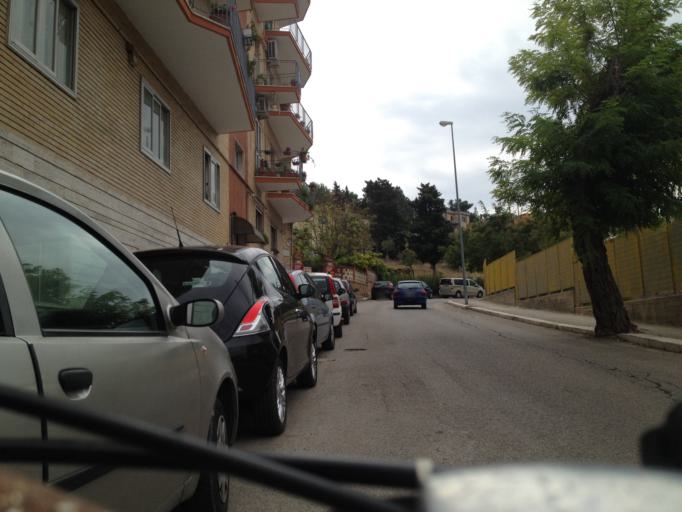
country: IT
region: Basilicate
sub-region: Provincia di Matera
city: Matera
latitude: 40.6642
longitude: 16.5999
